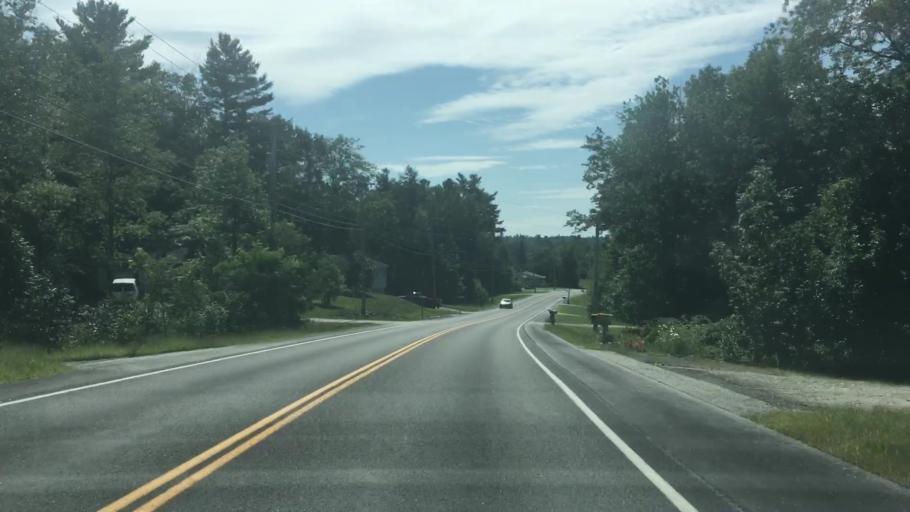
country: US
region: Maine
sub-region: Androscoggin County
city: Sabattus
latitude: 44.0767
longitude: -70.0795
